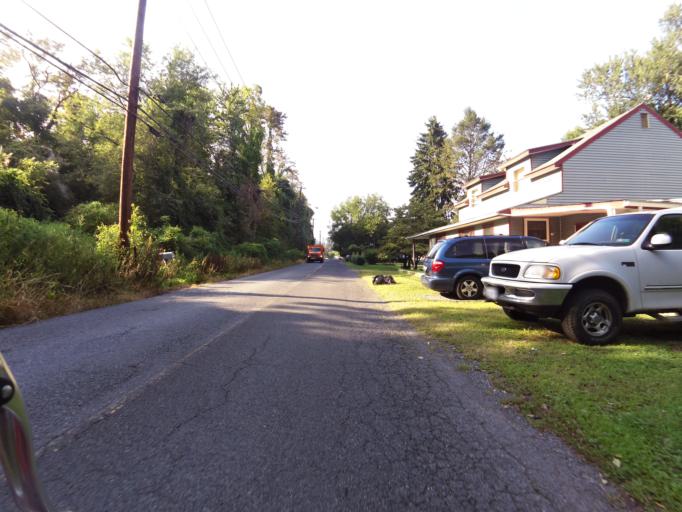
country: US
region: Pennsylvania
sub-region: Perry County
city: Marysville
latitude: 40.3355
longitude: -76.9227
